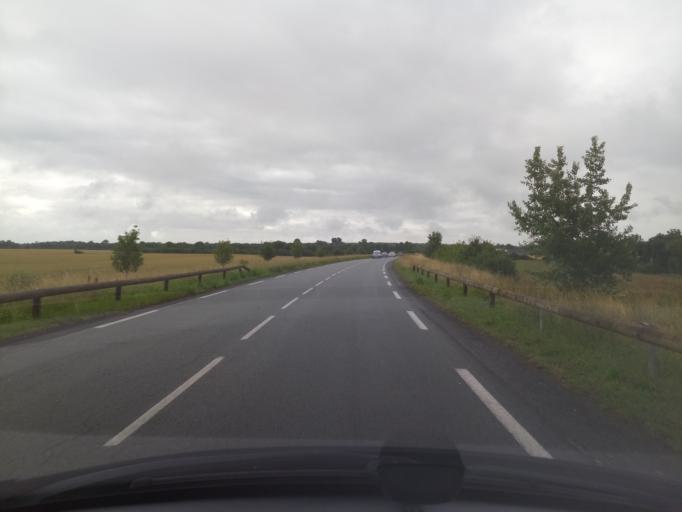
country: FR
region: Poitou-Charentes
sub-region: Departement de la Charente-Maritime
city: Courcon
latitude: 46.1944
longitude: -0.8647
